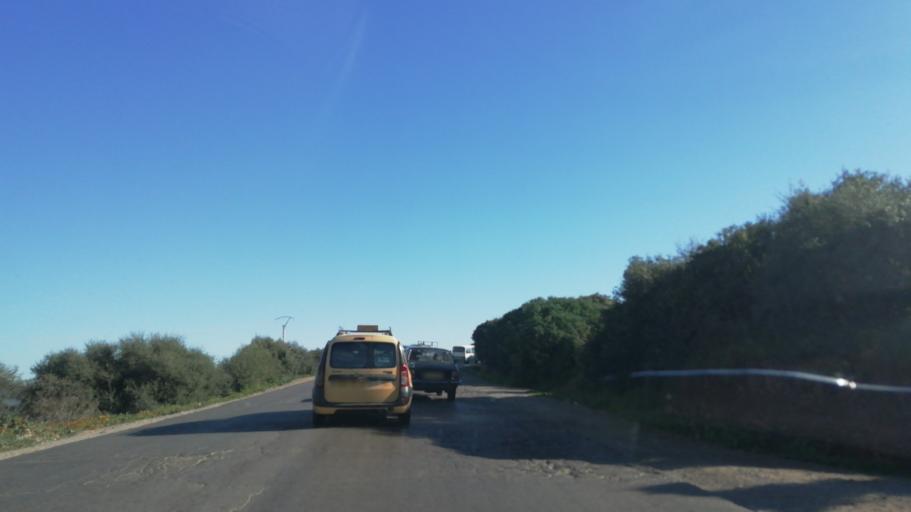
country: DZ
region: Relizane
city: Smala
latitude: 35.7005
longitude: 0.7766
